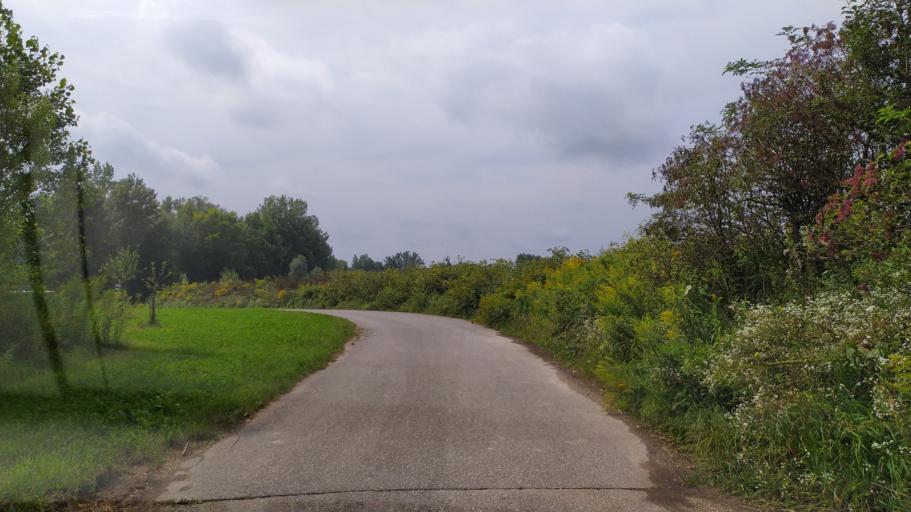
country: AT
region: Lower Austria
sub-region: Politischer Bezirk Amstetten
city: Zeillern
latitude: 48.1921
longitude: 14.7724
